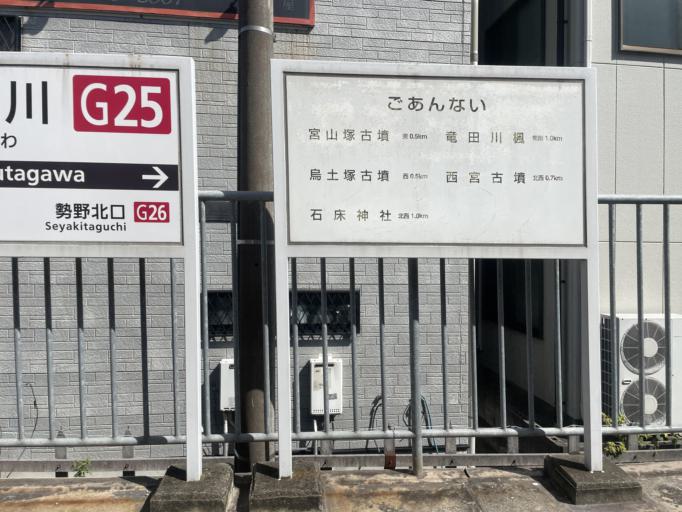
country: JP
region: Nara
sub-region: Ikoma-shi
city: Ikoma
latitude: 34.6170
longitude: 135.7046
